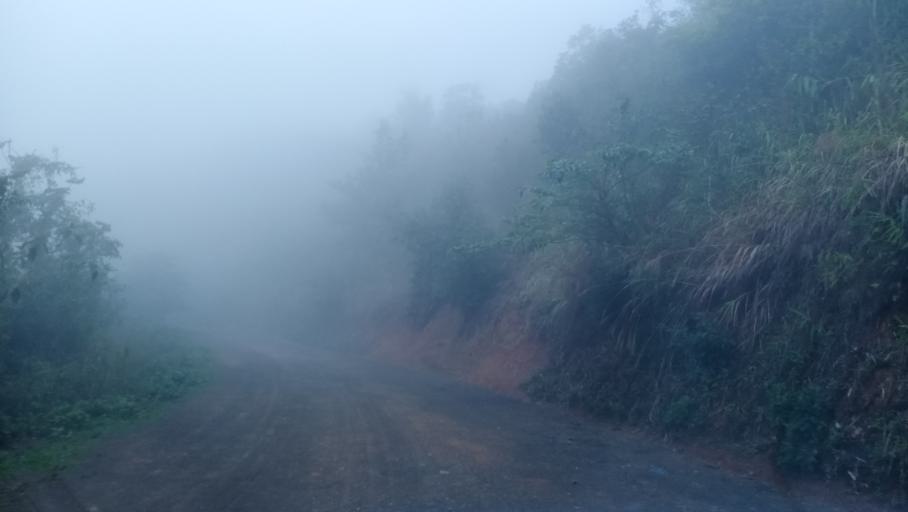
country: LA
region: Phongsali
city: Phongsali
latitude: 21.5002
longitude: 102.1728
